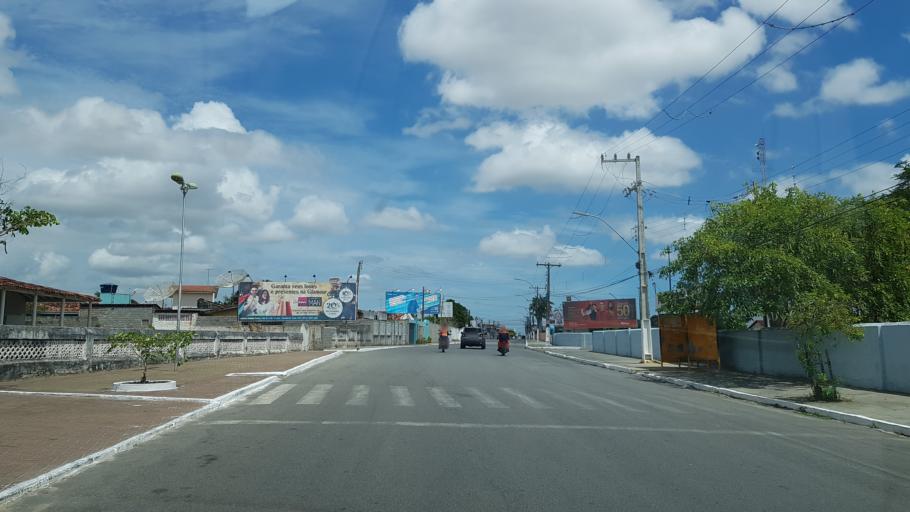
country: BR
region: Alagoas
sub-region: Penedo
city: Penedo
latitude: -10.2831
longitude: -36.5673
